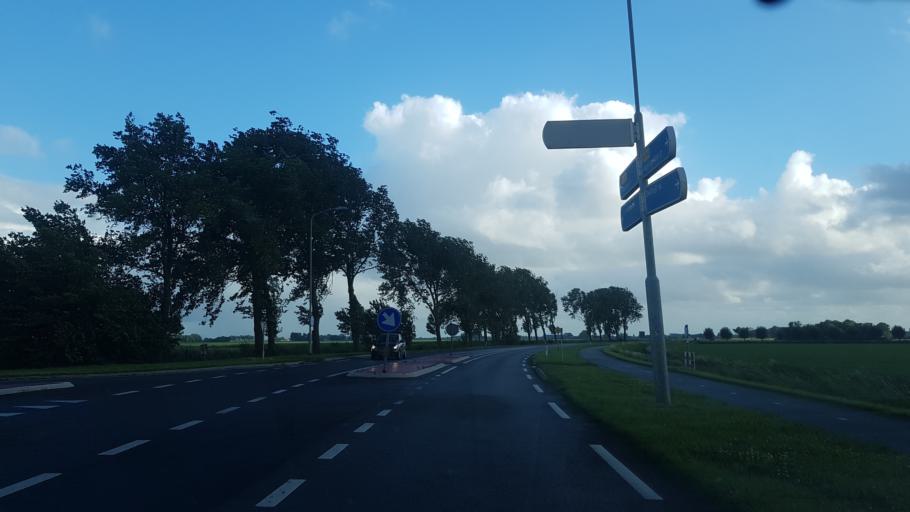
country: NL
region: Groningen
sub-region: Gemeente Slochteren
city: Slochteren
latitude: 53.2929
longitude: 6.7237
